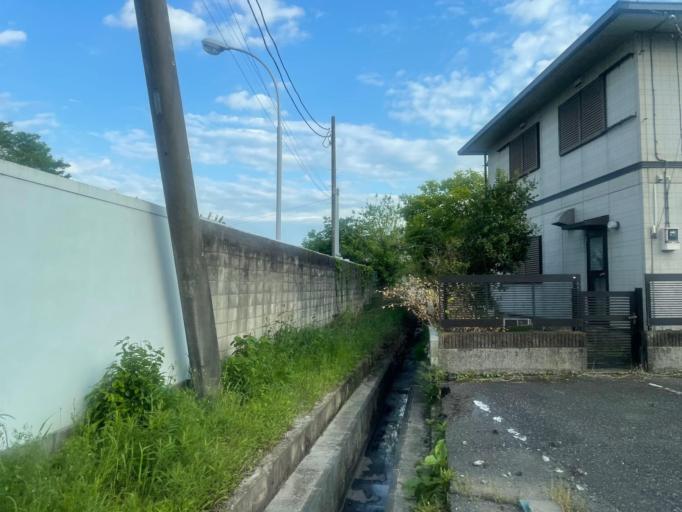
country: JP
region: Tochigi
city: Tochigi
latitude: 36.3794
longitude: 139.7277
